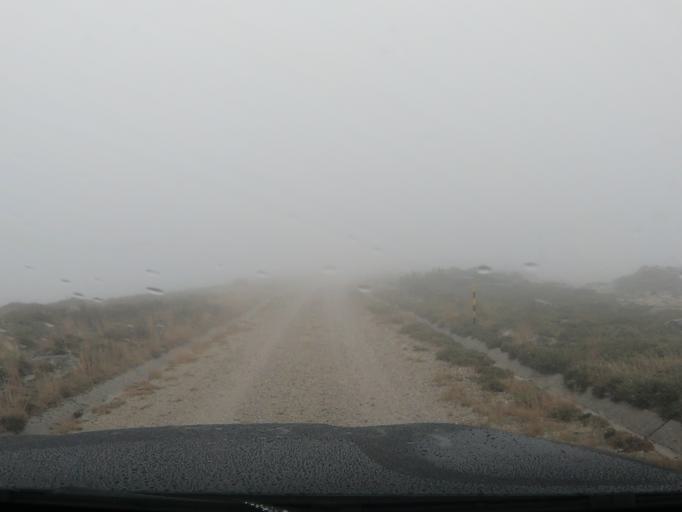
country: PT
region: Vila Real
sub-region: Vila Real
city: Vila Real
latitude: 41.3324
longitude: -7.8486
